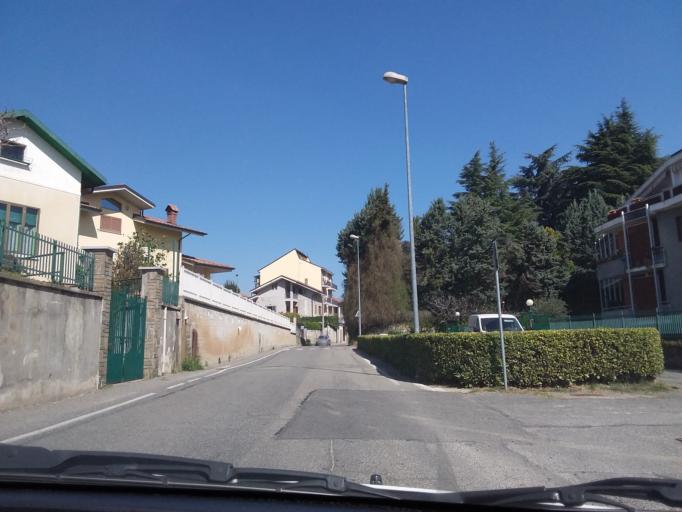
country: IT
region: Piedmont
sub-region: Provincia di Torino
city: Rivoli
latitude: 45.0616
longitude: 7.5158
